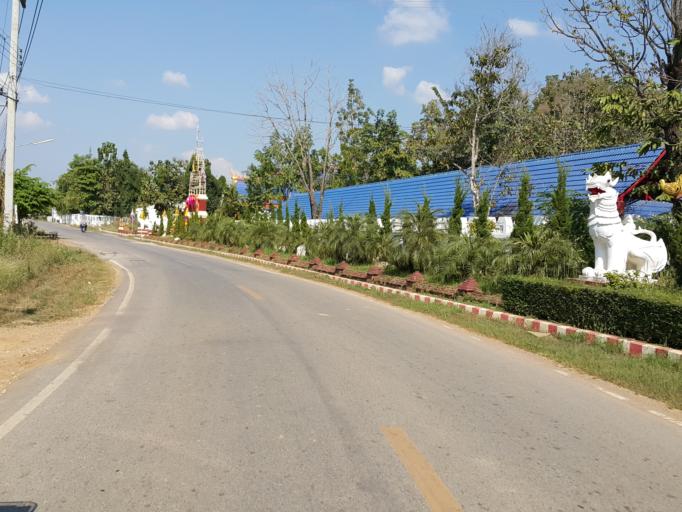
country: TH
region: Sukhothai
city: Thung Saliam
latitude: 17.3231
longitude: 99.5498
